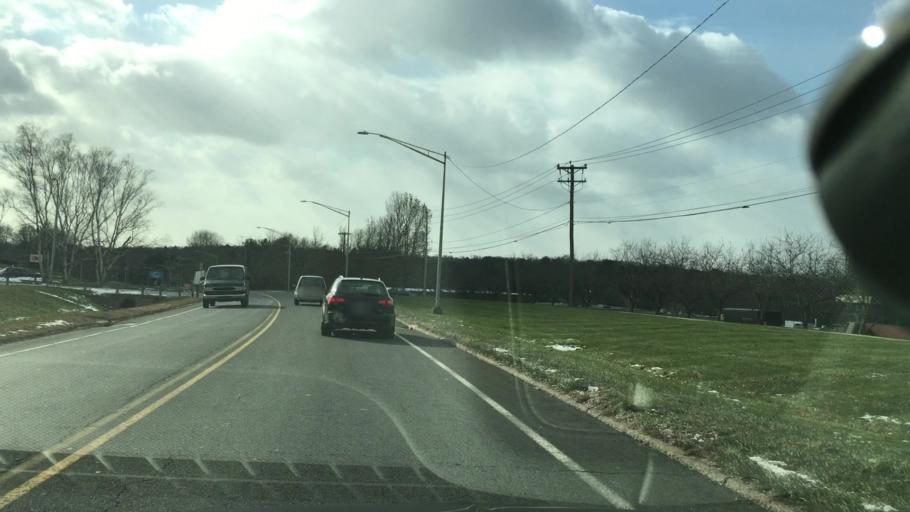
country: US
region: Connecticut
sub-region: New Haven County
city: Meriden
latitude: 41.5171
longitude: -72.7645
